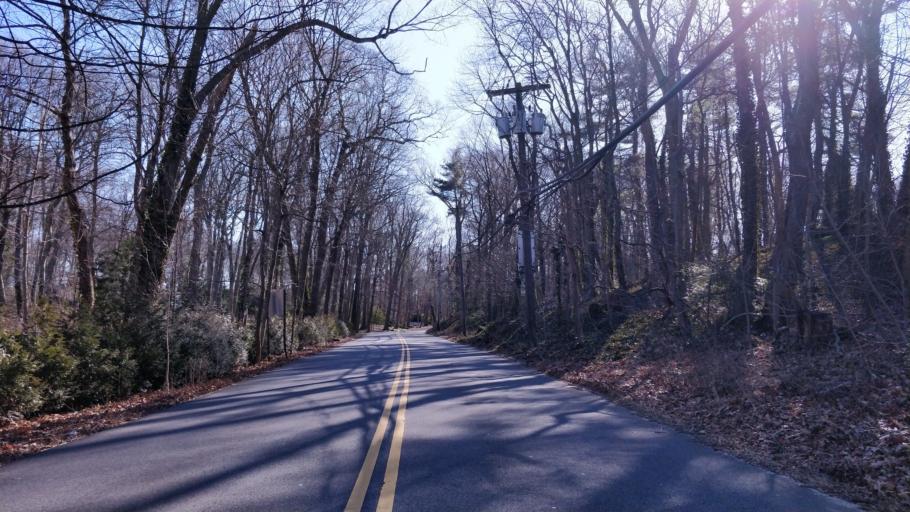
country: US
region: New York
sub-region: Nassau County
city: Old Brookville
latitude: 40.8162
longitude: -73.6043
